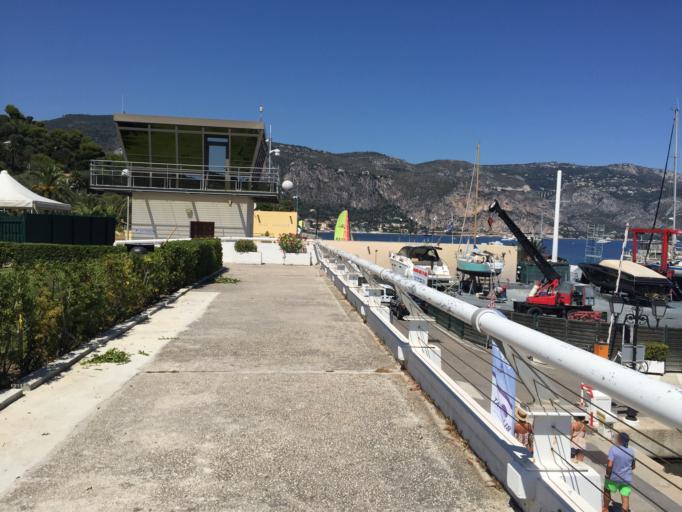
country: FR
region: Provence-Alpes-Cote d'Azur
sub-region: Departement des Alpes-Maritimes
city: Saint-Jean-Cap-Ferrat
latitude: 43.6910
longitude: 7.3339
